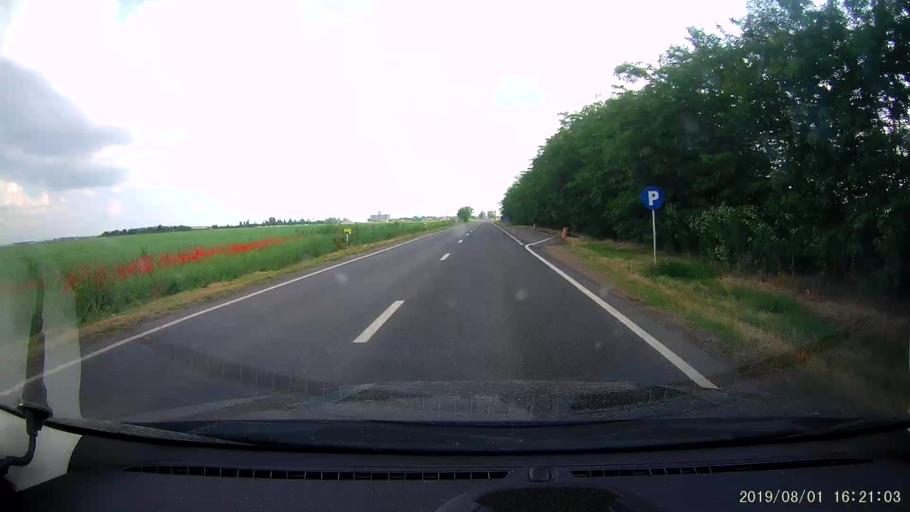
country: RO
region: Calarasi
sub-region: Municipiul Calarasi
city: Calarasi
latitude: 44.2213
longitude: 27.3407
